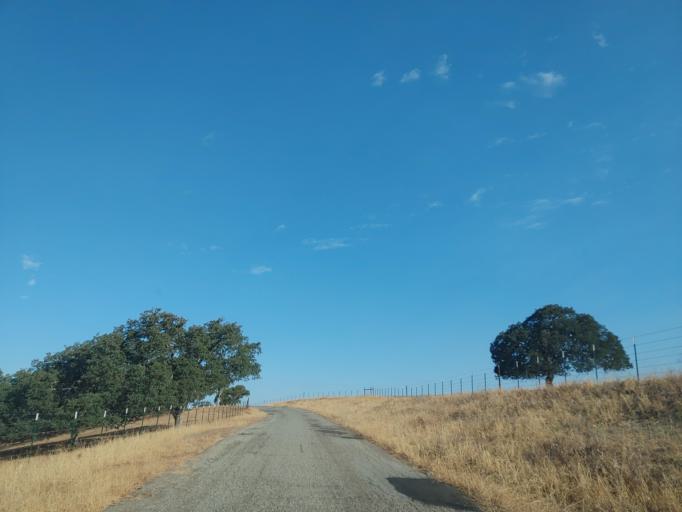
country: US
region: California
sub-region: San Benito County
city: Ridgemark
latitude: 36.7747
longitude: -121.2369
